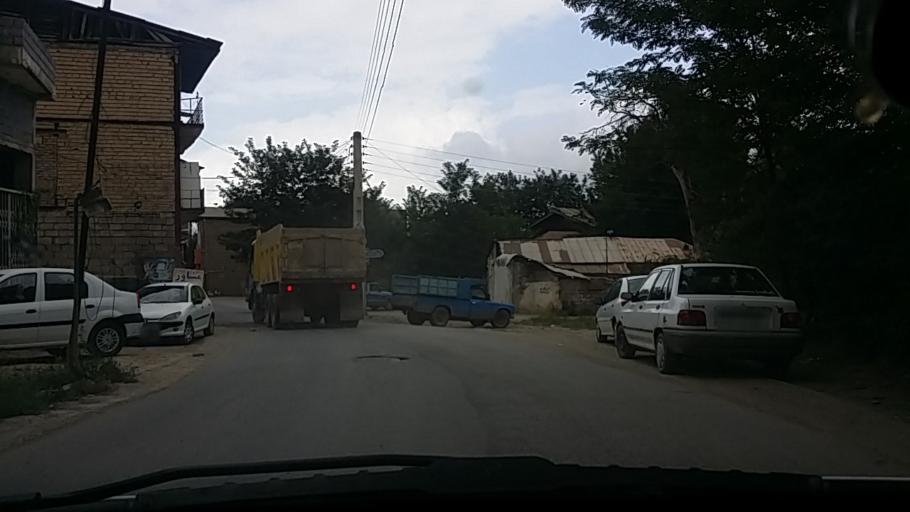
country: IR
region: Mazandaran
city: `Abbasabad
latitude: 36.5061
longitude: 51.1638
